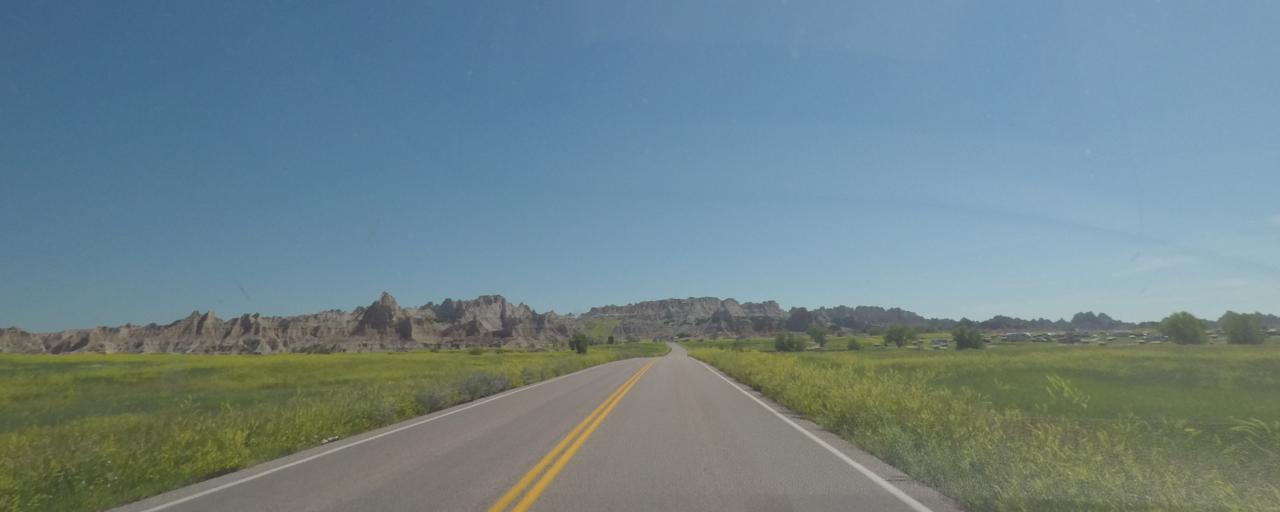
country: US
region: South Dakota
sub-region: Haakon County
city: Philip
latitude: 43.7432
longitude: -101.9552
